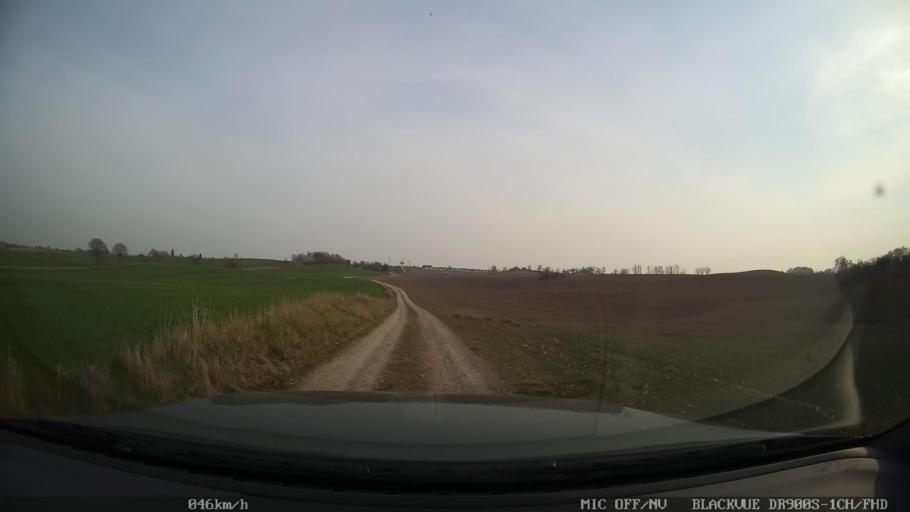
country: SE
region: Skane
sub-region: Ystads Kommun
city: Ystad
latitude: 55.4574
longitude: 13.7897
